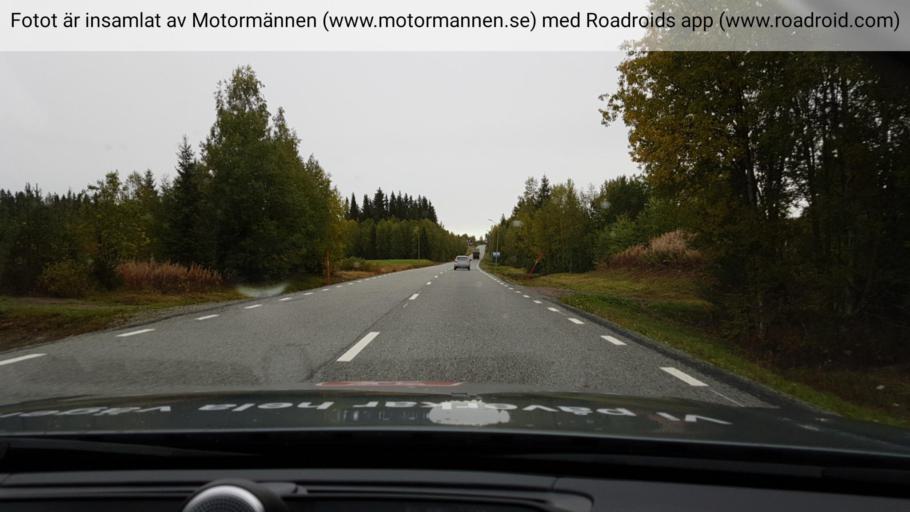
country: SE
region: Jaemtland
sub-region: Stroemsunds Kommun
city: Stroemsund
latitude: 64.0507
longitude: 15.5442
